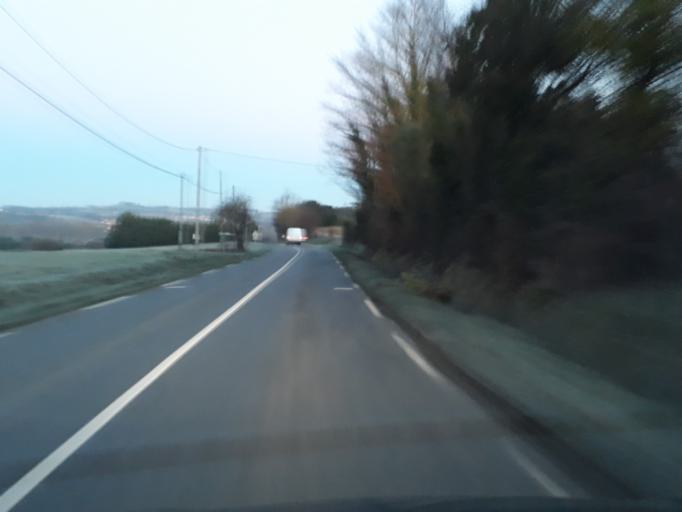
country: FR
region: Midi-Pyrenees
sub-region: Departement du Gers
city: Samatan
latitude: 43.4789
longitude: 0.9399
